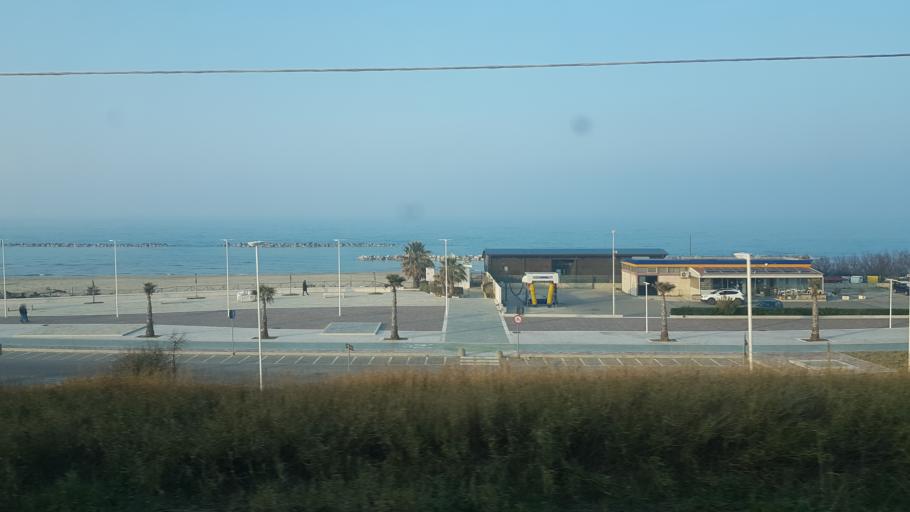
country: IT
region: Molise
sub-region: Provincia di Campobasso
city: Termoli
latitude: 42.0068
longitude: 14.9697
